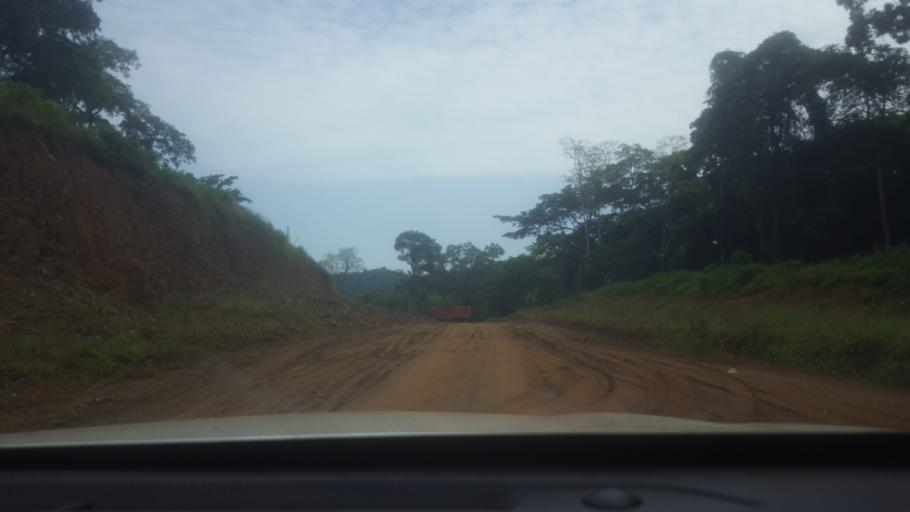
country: ET
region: Southern Nations, Nationalities, and People's Region
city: Tippi
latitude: 7.5232
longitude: 34.9920
